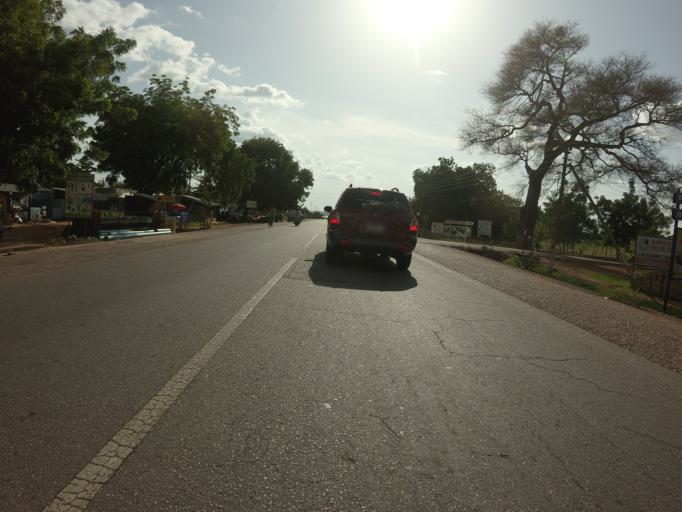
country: GH
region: Upper East
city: Bolgatanga
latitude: 10.8030
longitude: -0.8682
